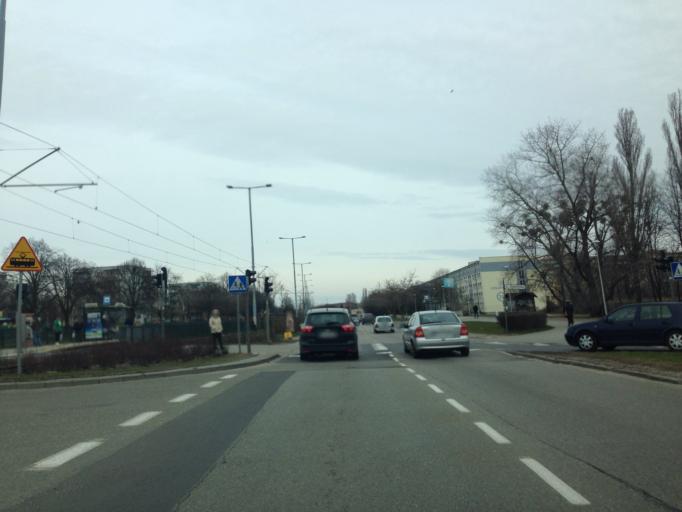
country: PL
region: Pomeranian Voivodeship
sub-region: Sopot
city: Sopot
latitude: 54.4123
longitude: 18.5881
